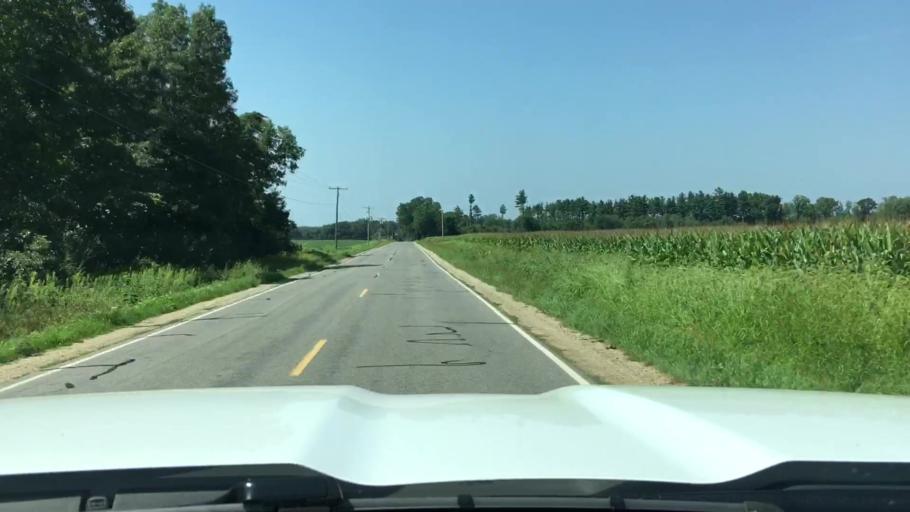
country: US
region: Michigan
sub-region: Saint Joseph County
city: Three Rivers
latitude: 41.9985
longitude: -85.5906
